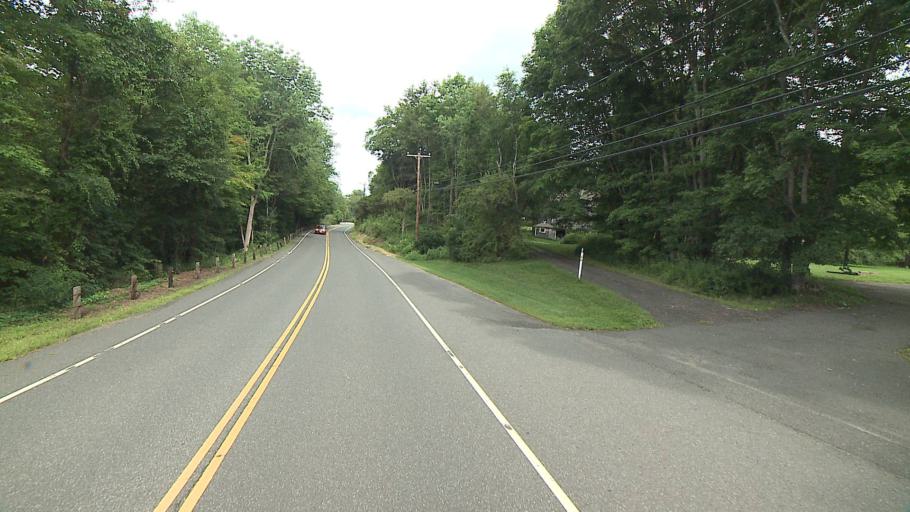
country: US
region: Connecticut
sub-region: Litchfield County
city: Woodbury
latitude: 41.5791
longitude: -73.2420
